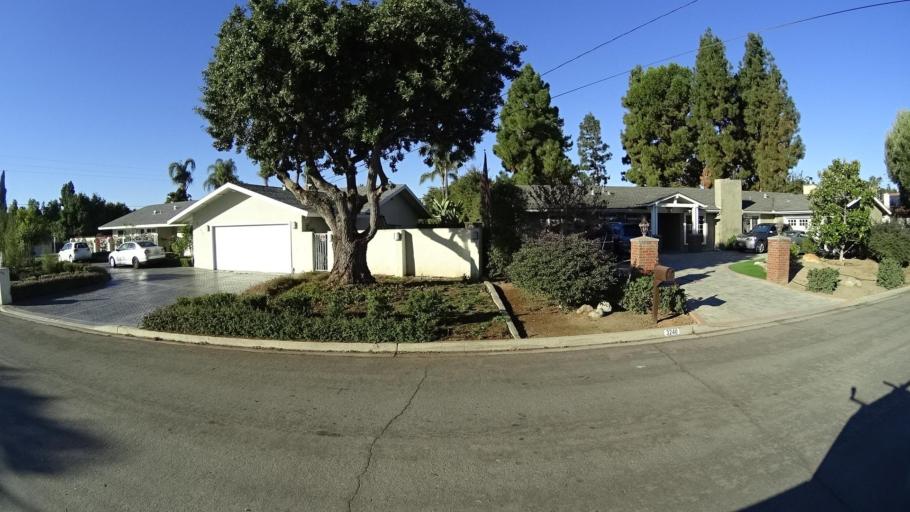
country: US
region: California
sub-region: San Diego County
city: Bonita
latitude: 32.6741
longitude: -117.0271
